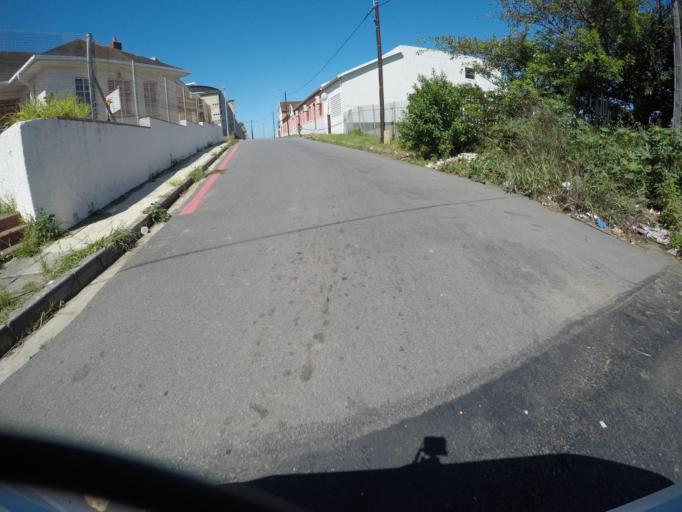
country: ZA
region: Eastern Cape
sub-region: Buffalo City Metropolitan Municipality
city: East London
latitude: -33.0218
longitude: 27.9032
